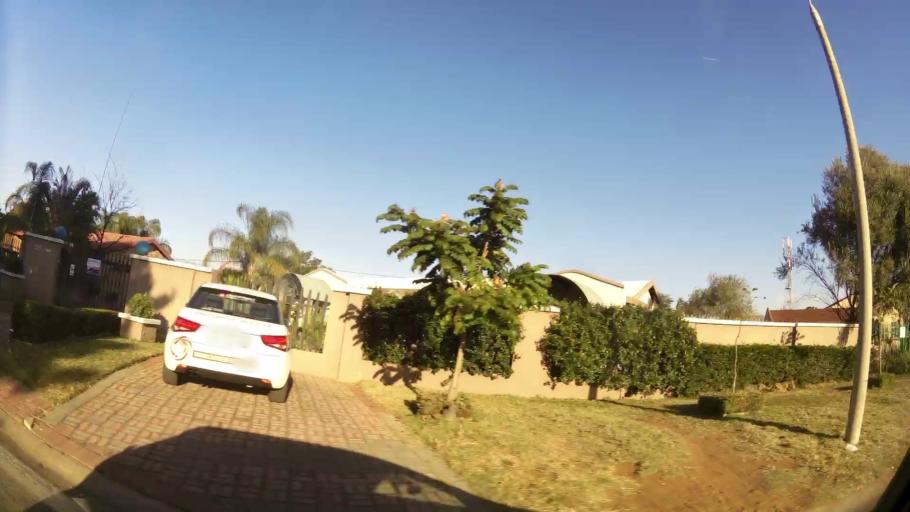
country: ZA
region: North-West
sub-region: Bojanala Platinum District Municipality
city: Rustenburg
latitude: -25.6793
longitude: 27.2176
